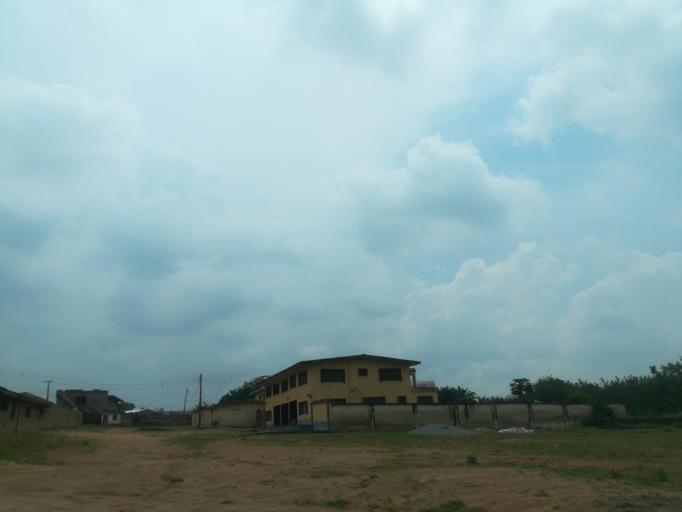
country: NG
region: Oyo
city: Ibadan
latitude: 7.4258
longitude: 3.9330
